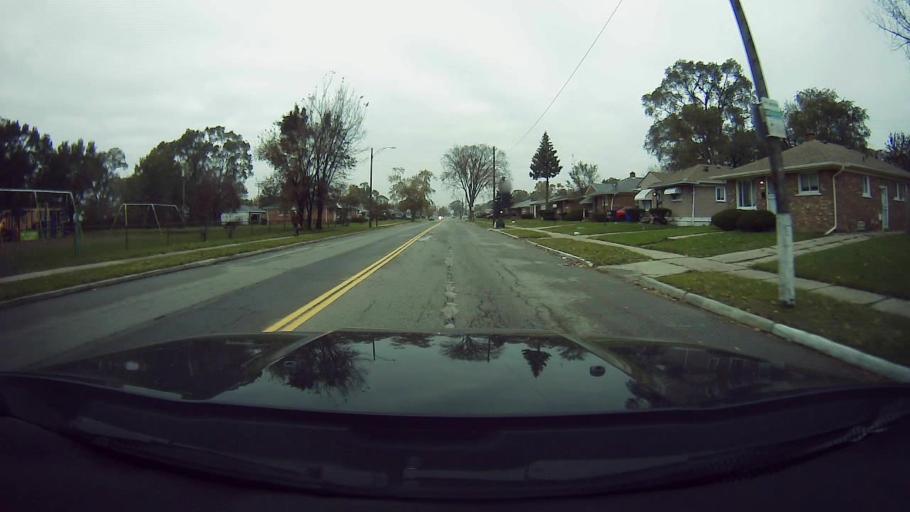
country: US
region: Michigan
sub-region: Wayne County
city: Highland Park
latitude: 42.4285
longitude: -83.0827
